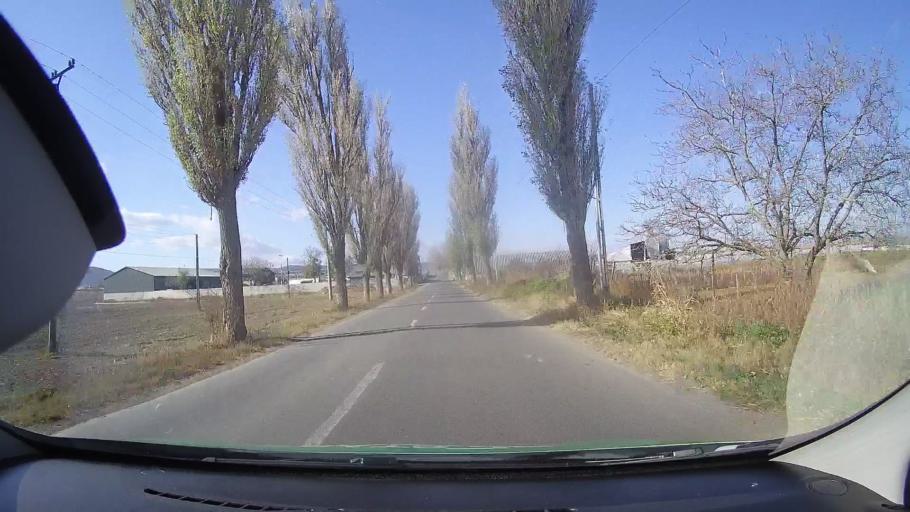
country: RO
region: Tulcea
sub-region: Comuna Sarichioi
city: Enisala
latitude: 44.8785
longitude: 28.8061
